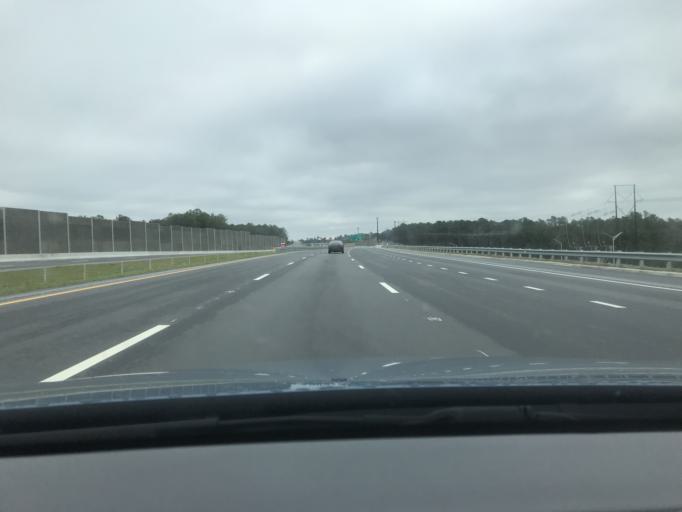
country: US
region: North Carolina
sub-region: Cumberland County
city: Fort Bragg
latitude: 35.1072
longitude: -79.0070
